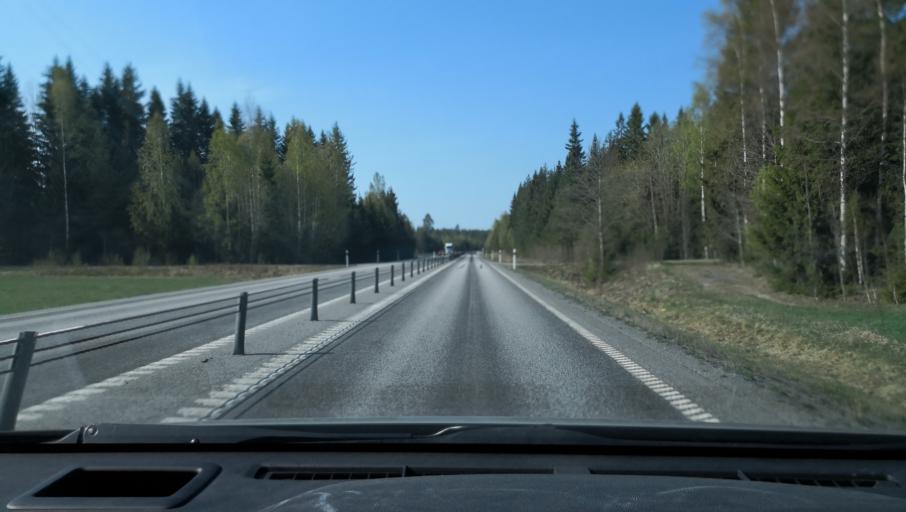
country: SE
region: Uppsala
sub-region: Heby Kommun
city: Tarnsjo
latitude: 60.1756
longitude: 16.9511
